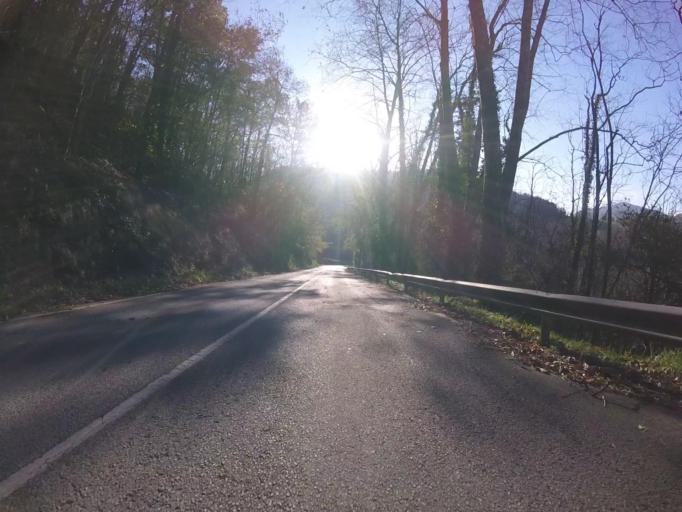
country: ES
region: Navarre
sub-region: Provincia de Navarra
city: Lesaka
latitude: 43.2402
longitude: -1.6725
